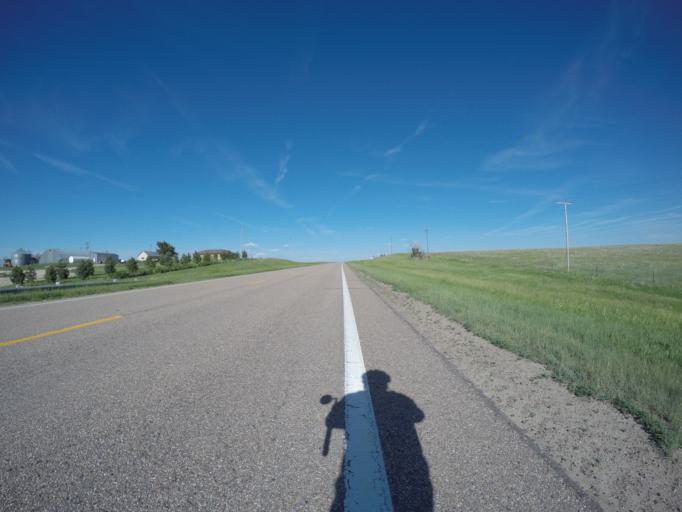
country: US
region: Kansas
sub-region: Cheyenne County
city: Saint Francis
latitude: 39.7564
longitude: -102.0148
